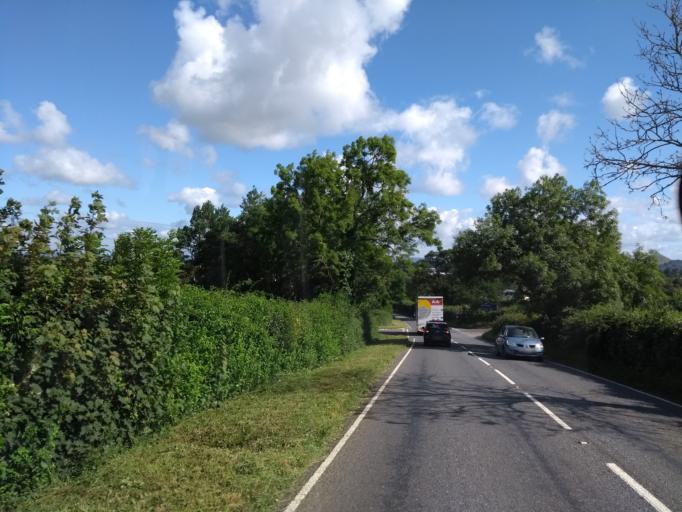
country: GB
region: England
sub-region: Somerset
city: Street
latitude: 51.1151
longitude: -2.7324
